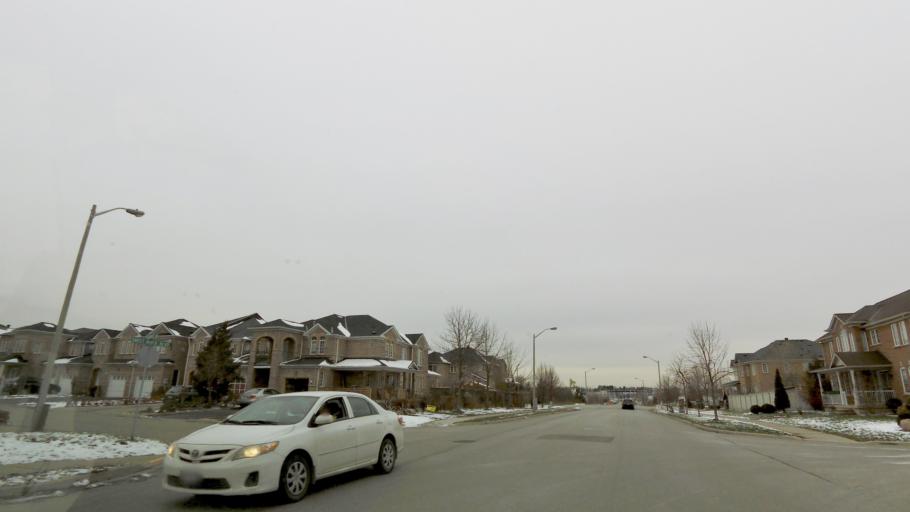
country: CA
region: Ontario
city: Vaughan
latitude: 43.8322
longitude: -79.5395
